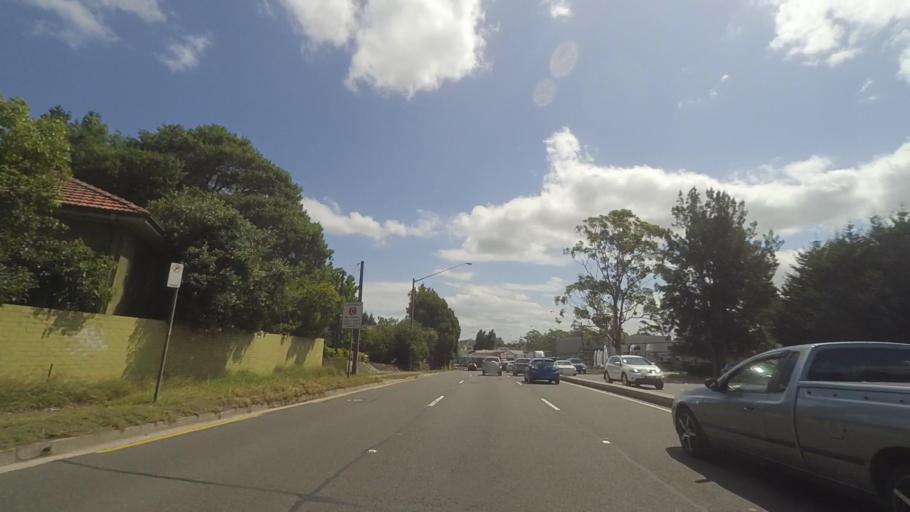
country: AU
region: New South Wales
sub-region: Hornsby Shire
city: Pennant Hills
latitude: -33.7355
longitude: 151.0759
